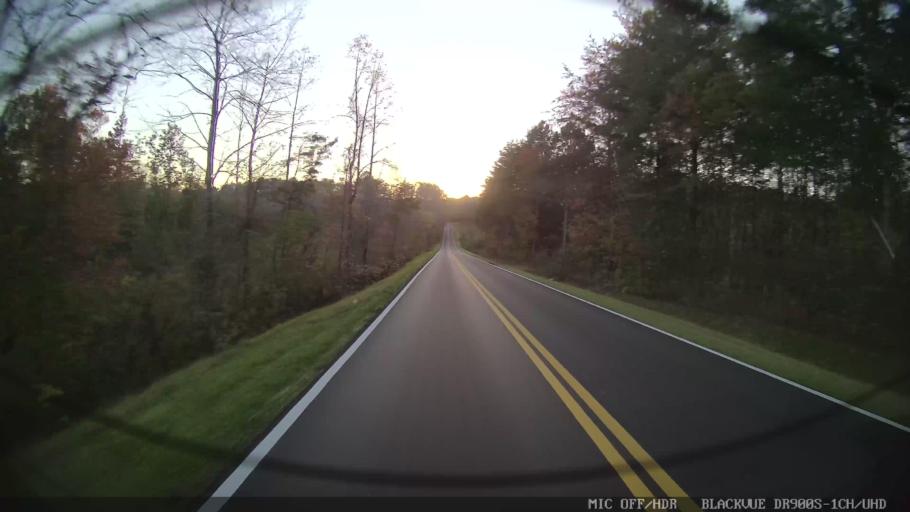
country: US
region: Georgia
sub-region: Union County
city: Blairsville
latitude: 34.8534
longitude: -83.9117
